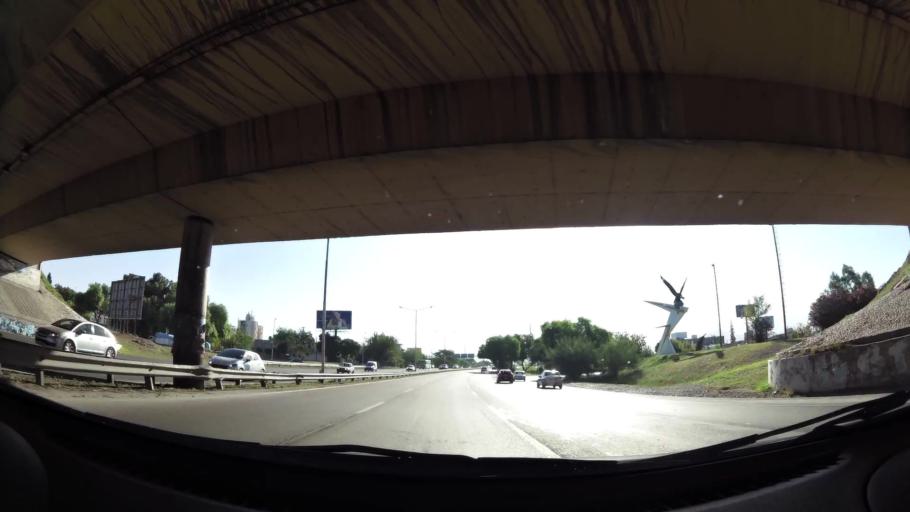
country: AR
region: Mendoza
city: Mendoza
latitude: -32.8976
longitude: -68.8192
